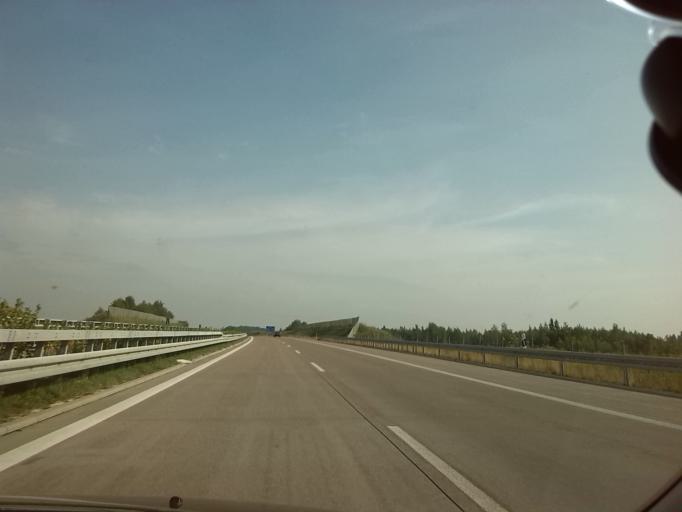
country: DE
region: Saxony
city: Penig
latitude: 50.9486
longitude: 12.6906
